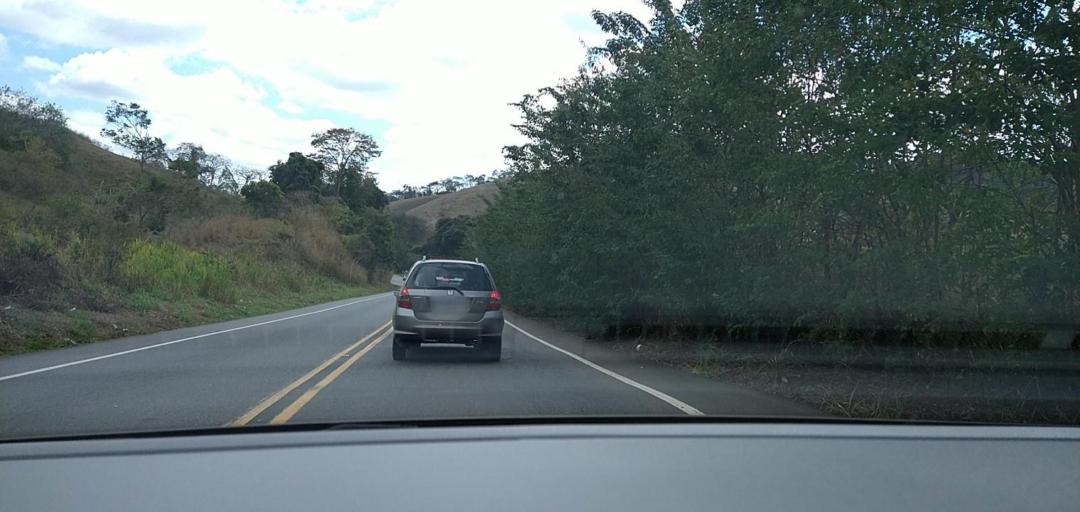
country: BR
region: Minas Gerais
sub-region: Ponte Nova
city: Ponte Nova
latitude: -20.5018
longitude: -42.8766
